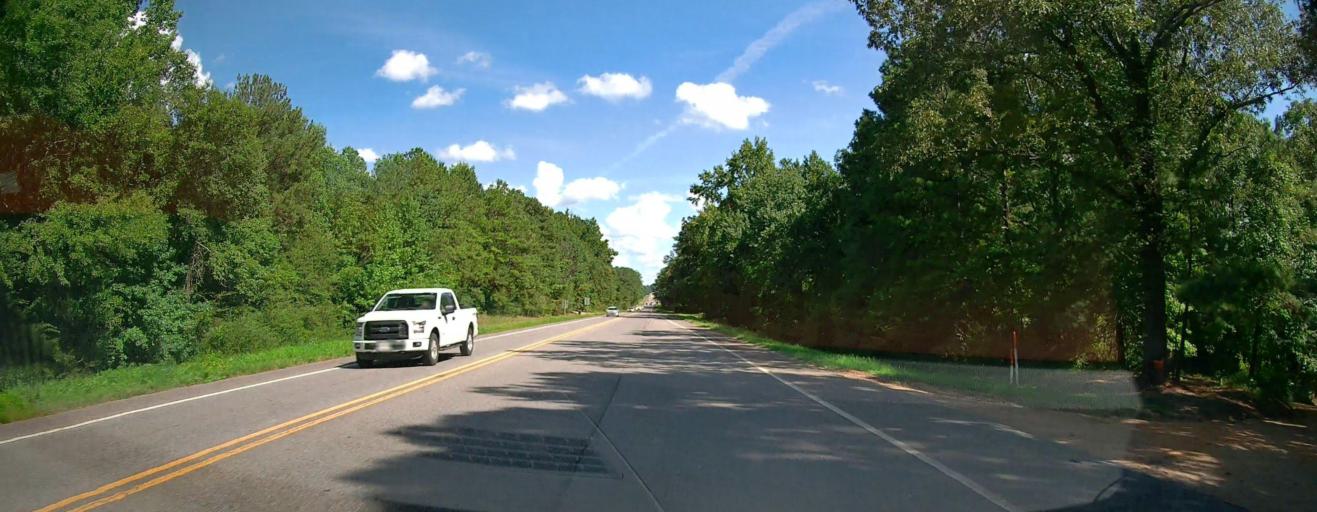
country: US
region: Alabama
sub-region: Pickens County
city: Gordo
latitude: 33.3100
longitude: -87.8902
